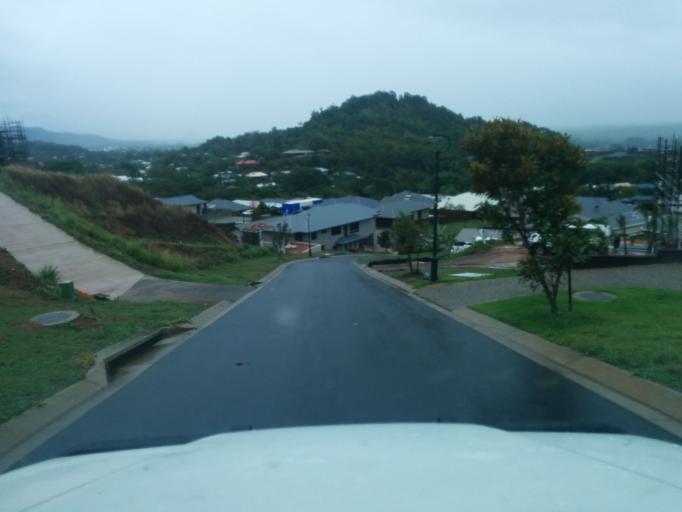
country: AU
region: Queensland
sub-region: Cairns
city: Woree
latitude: -16.9754
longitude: 145.7326
